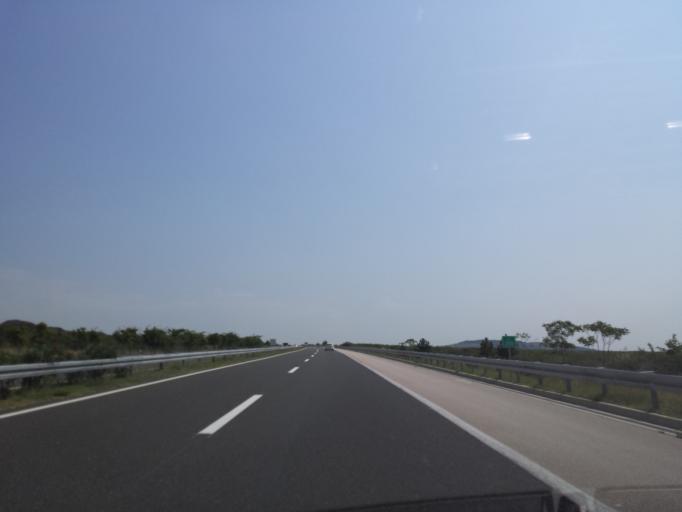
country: HR
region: Zadarska
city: Galovac
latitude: 44.0970
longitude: 15.4747
